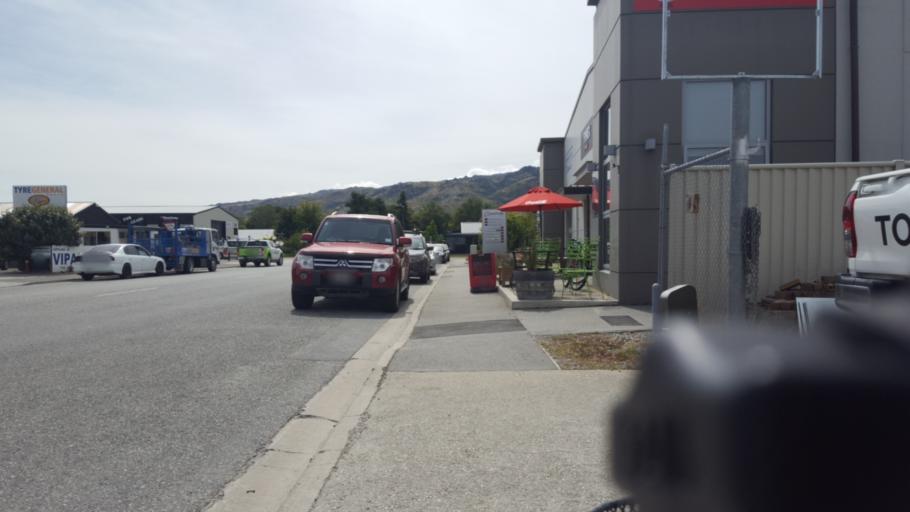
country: NZ
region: Otago
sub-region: Queenstown-Lakes District
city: Wanaka
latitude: -45.0496
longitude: 169.1938
